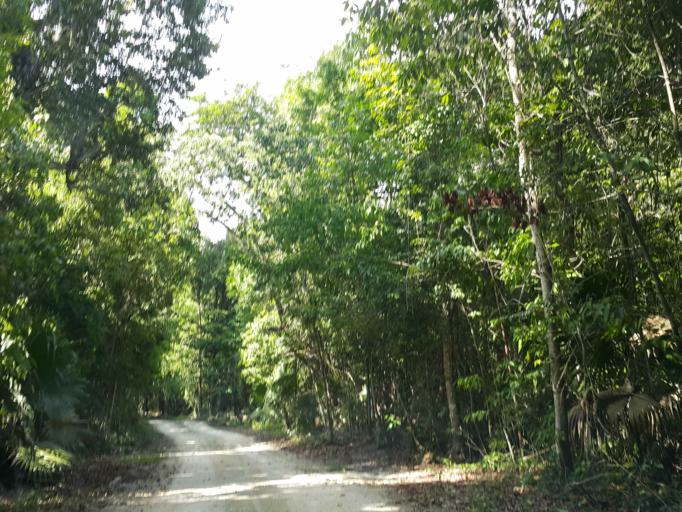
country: MX
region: Quintana Roo
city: Leona Vicario
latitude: 20.8698
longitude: -87.0458
